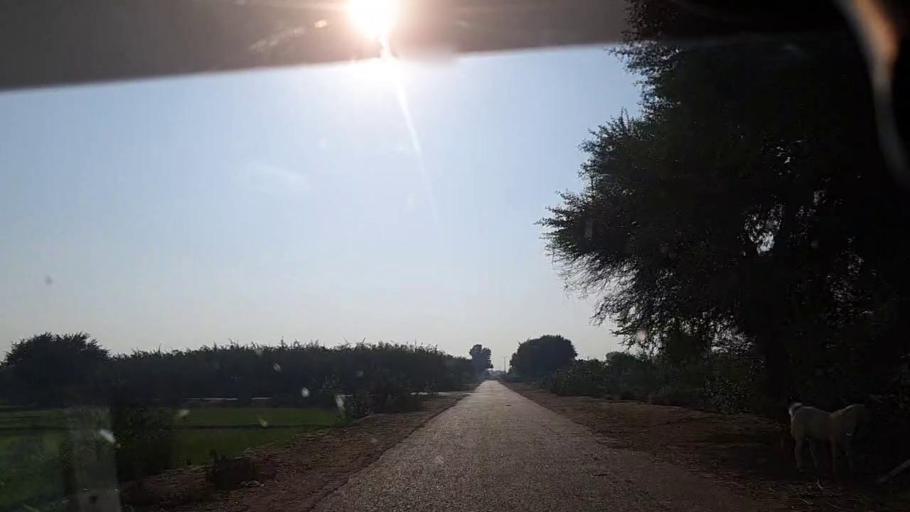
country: PK
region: Sindh
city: Sobhadero
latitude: 27.2394
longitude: 68.2826
